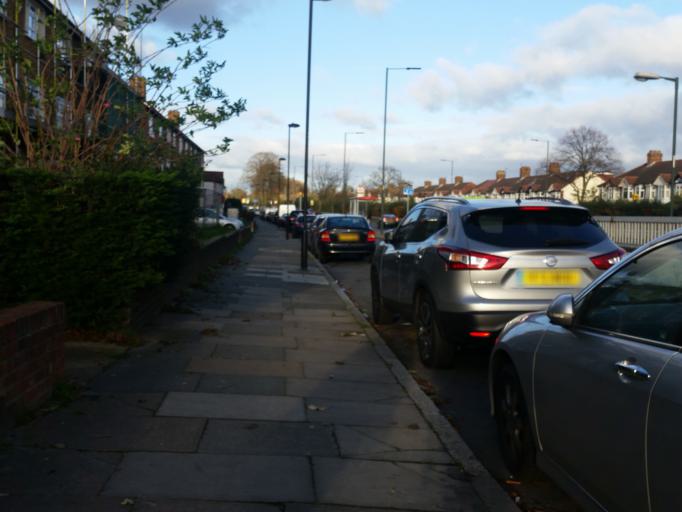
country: GB
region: England
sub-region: Greater London
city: Enfield
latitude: 51.6221
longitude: -0.0829
